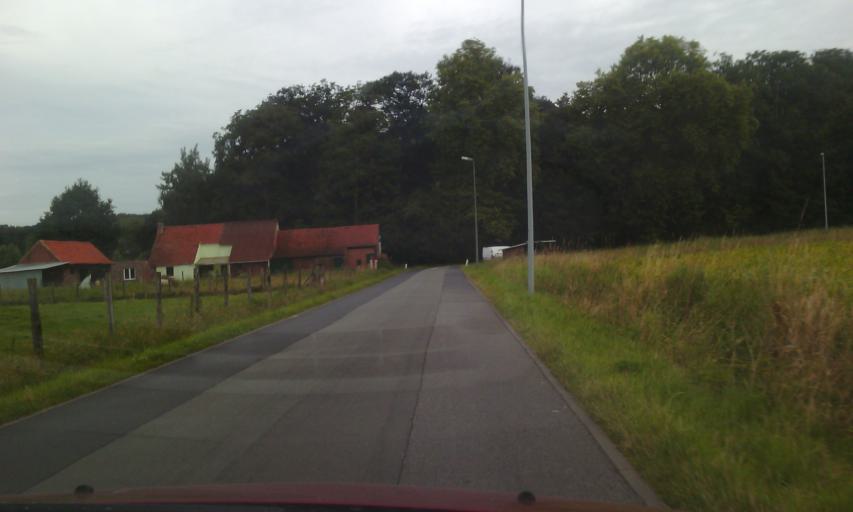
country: BE
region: Flanders
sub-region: Provincie Oost-Vlaanderen
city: Zele
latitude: 51.0803
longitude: 4.0359
